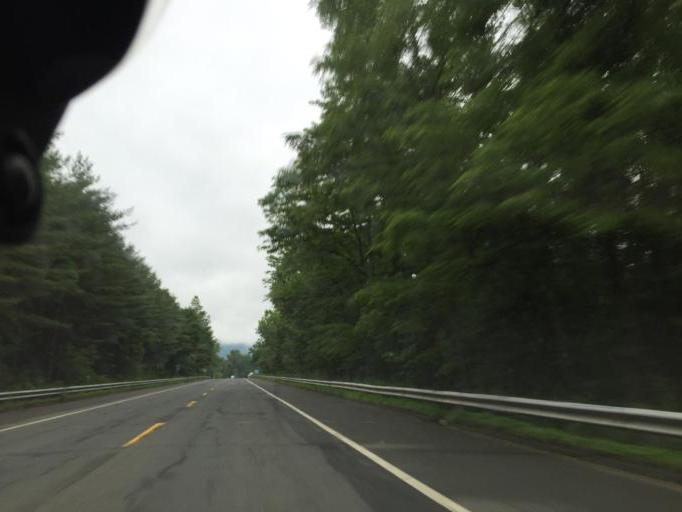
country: US
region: Connecticut
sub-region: Litchfield County
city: Canaan
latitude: 42.0499
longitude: -73.3261
